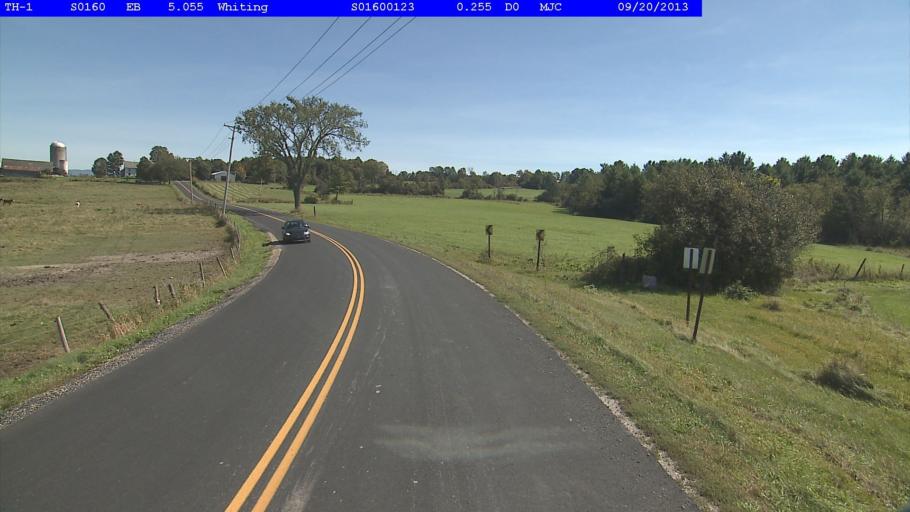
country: US
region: Vermont
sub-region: Rutland County
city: Brandon
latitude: 43.8621
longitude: -73.2204
